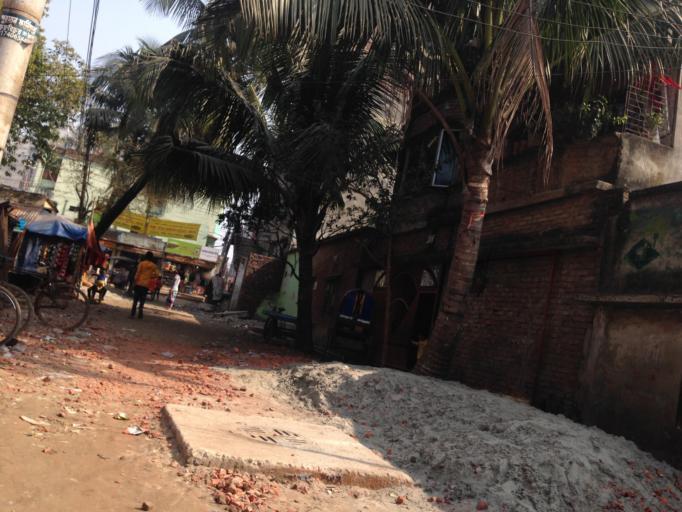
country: BD
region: Dhaka
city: Azimpur
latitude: 23.8046
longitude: 90.3462
